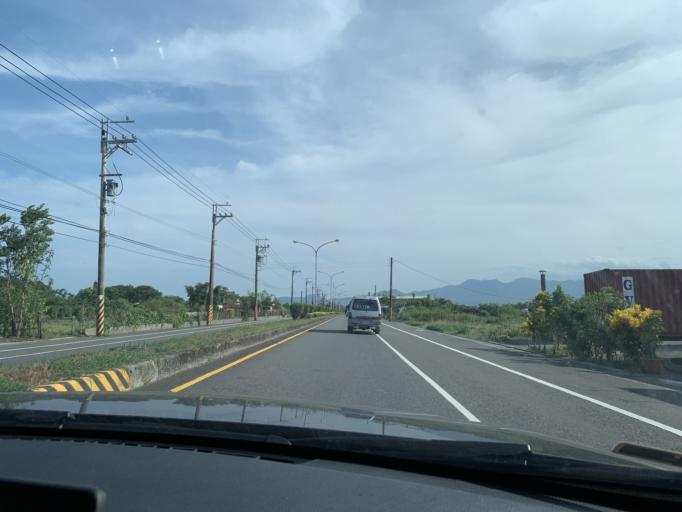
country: TW
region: Taiwan
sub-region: Yilan
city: Yilan
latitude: 24.7433
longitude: 121.8165
